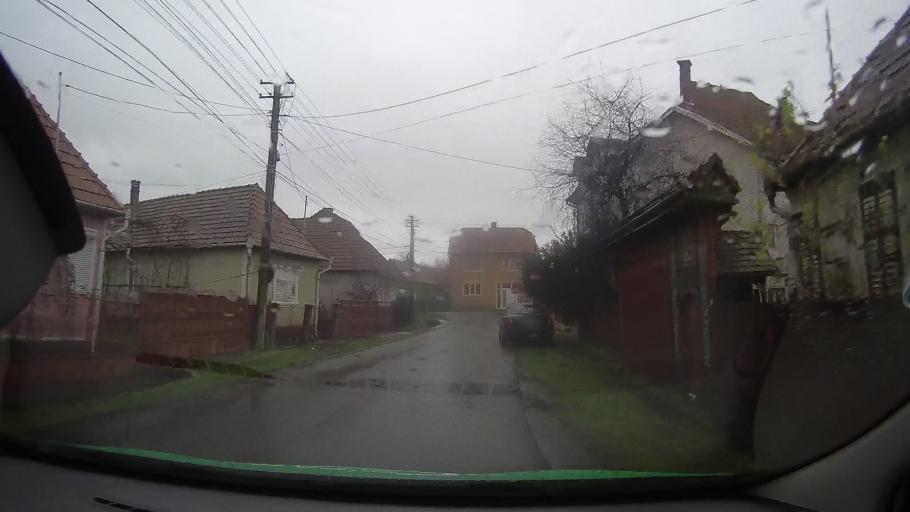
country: RO
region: Mures
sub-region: Comuna Alunis
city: Alunis
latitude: 46.8978
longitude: 24.8230
